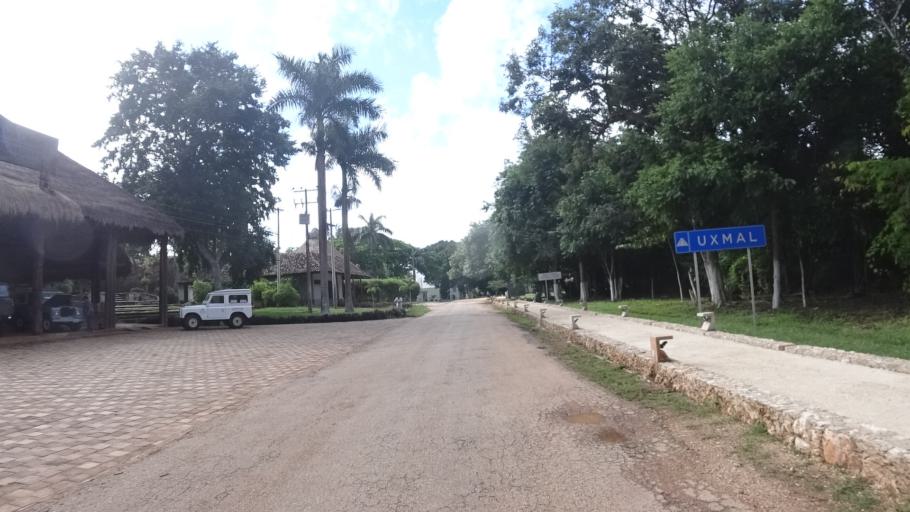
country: MX
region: Yucatan
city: Santa Elena
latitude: 20.3622
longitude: -89.7682
